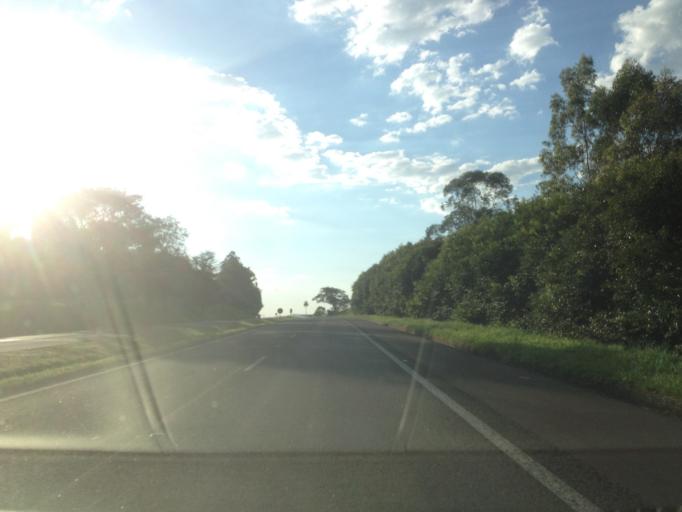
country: BR
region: Sao Paulo
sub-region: Brotas
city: Brotas
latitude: -22.2520
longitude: -48.2478
